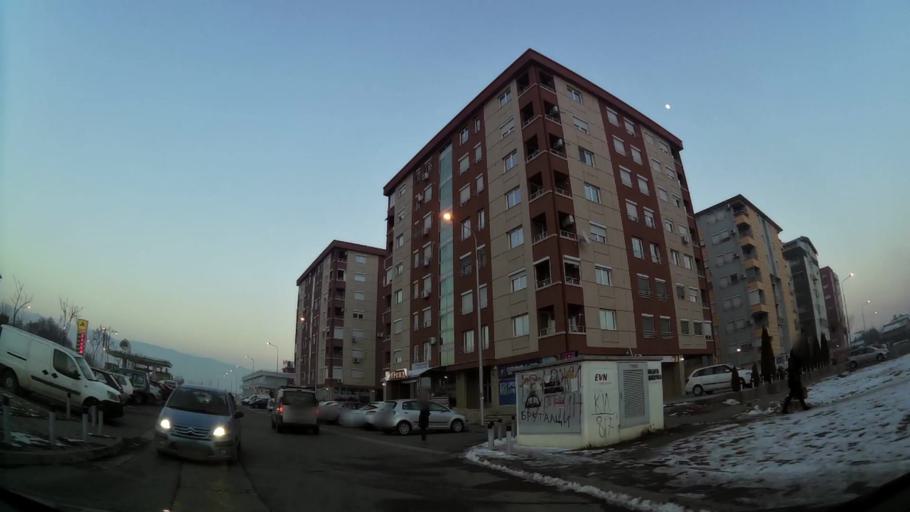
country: MK
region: Kisela Voda
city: Usje
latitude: 41.9832
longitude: 21.4825
